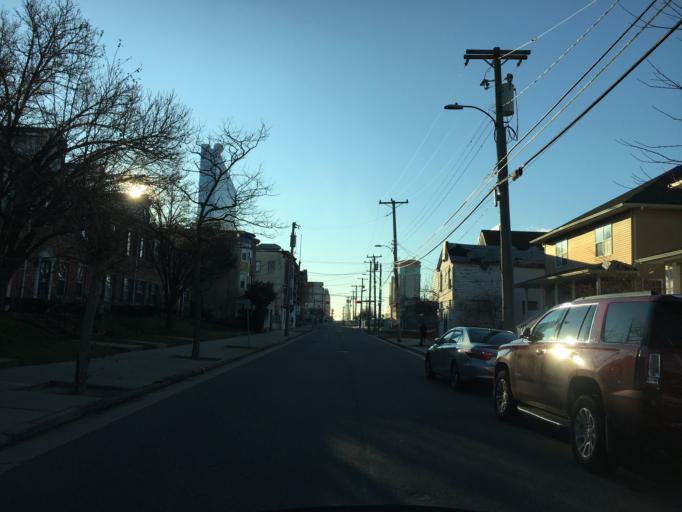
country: US
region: New Jersey
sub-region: Atlantic County
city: Atlantic City
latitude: 39.3681
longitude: -74.4209
